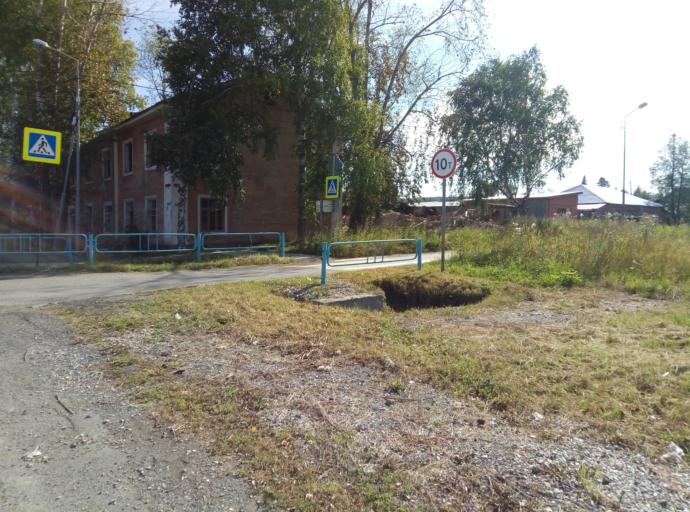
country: RU
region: Sverdlovsk
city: Karpinsk
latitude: 59.7766
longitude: 59.9814
